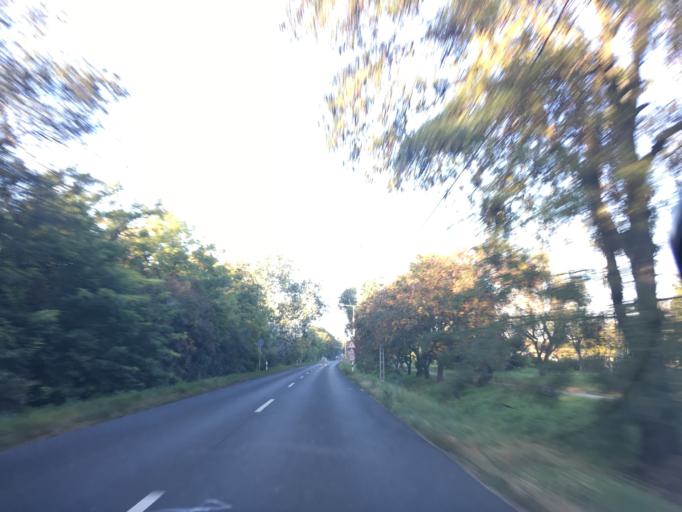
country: HU
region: Pest
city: Szazhalombatta
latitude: 47.3061
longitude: 18.8958
